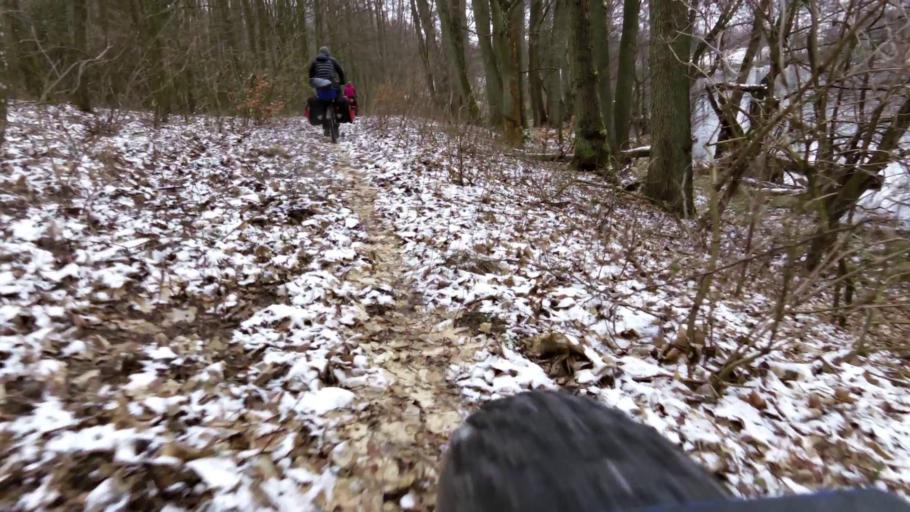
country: PL
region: West Pomeranian Voivodeship
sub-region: Powiat walecki
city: Miroslawiec
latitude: 53.3502
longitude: 16.2657
